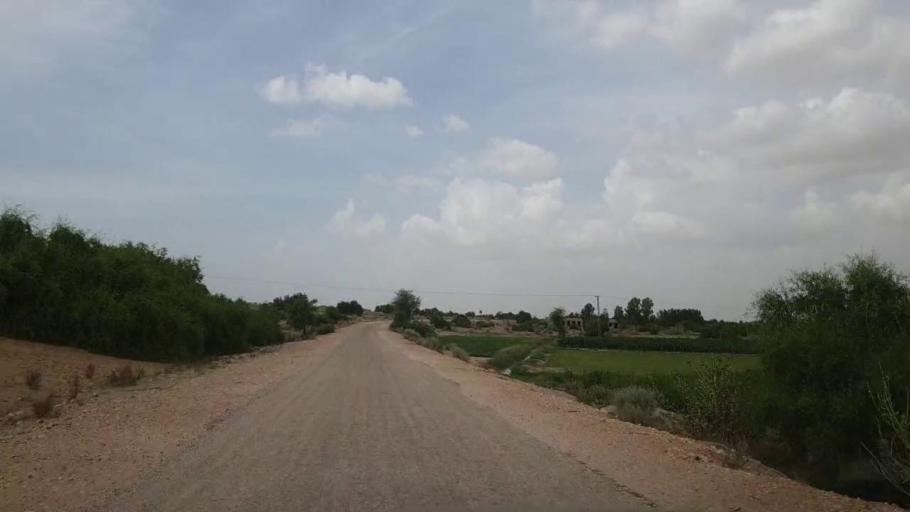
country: PK
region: Sindh
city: Kot Diji
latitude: 27.2129
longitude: 69.0832
